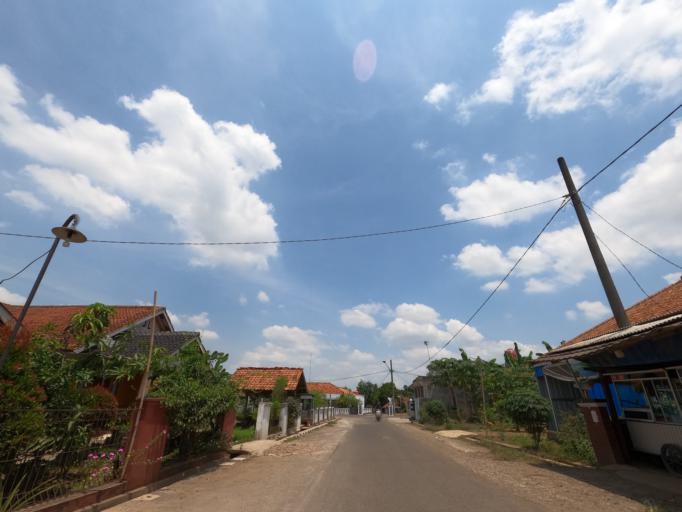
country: ID
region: West Java
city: Pamanukan
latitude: -6.5189
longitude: 107.7774
